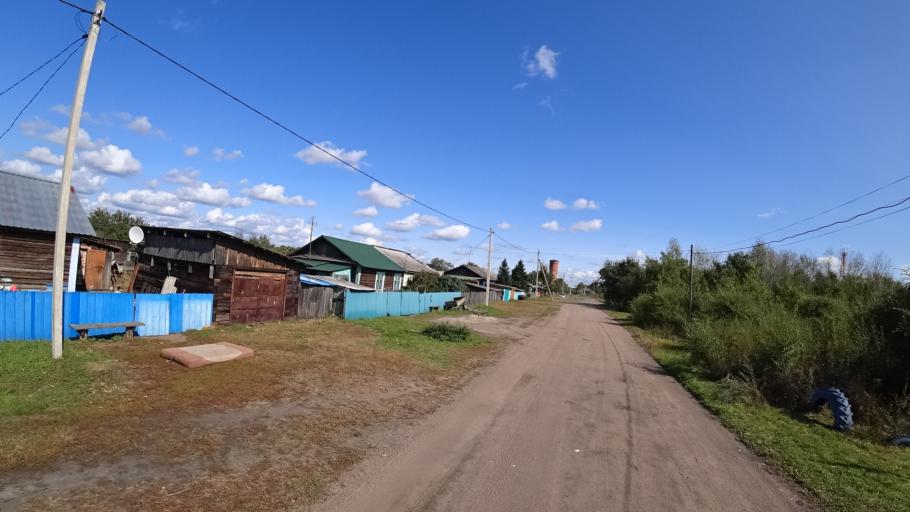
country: RU
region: Amur
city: Arkhara
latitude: 49.4048
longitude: 130.1371
